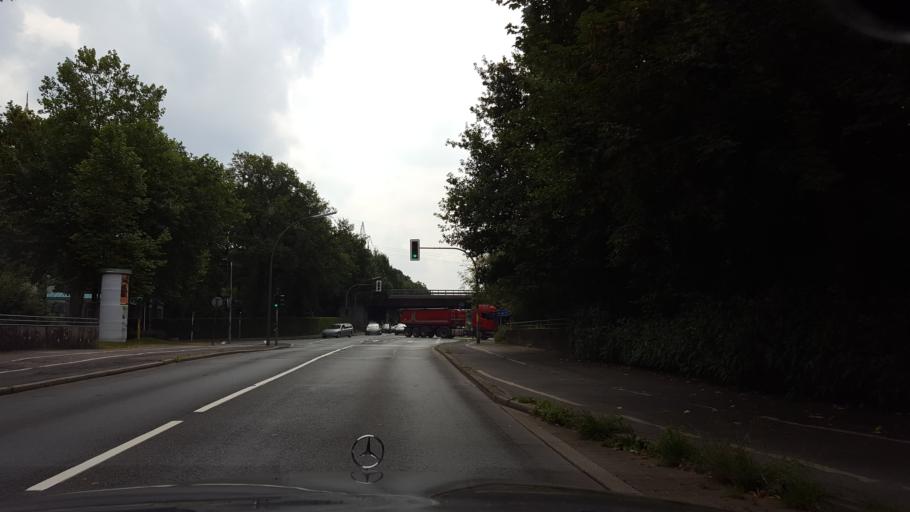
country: DE
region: North Rhine-Westphalia
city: Marl
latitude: 51.6798
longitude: 7.1230
